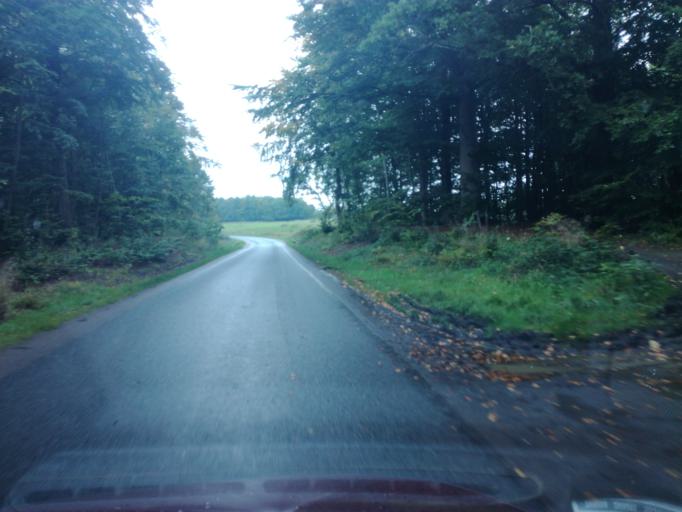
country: DK
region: South Denmark
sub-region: Fredericia Kommune
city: Fredericia
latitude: 55.6232
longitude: 9.8418
